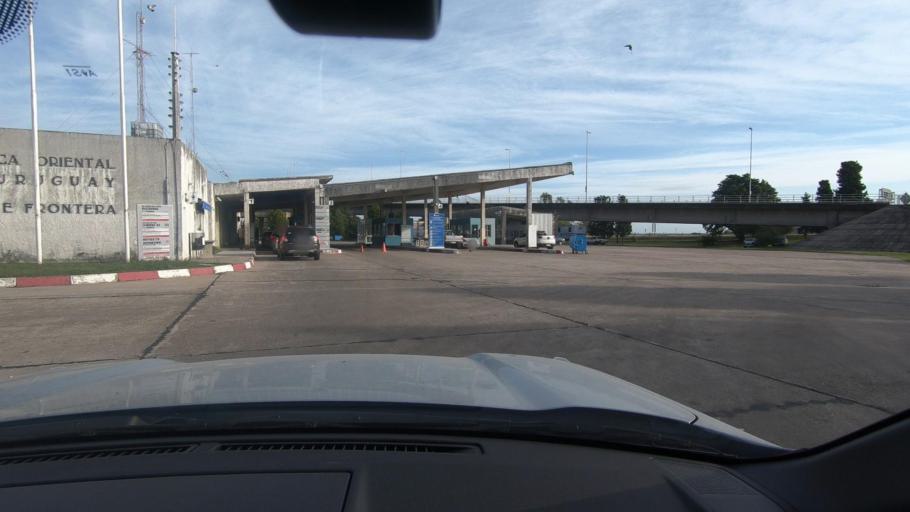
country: AR
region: Entre Rios
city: Colon
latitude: -32.2600
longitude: -58.1339
